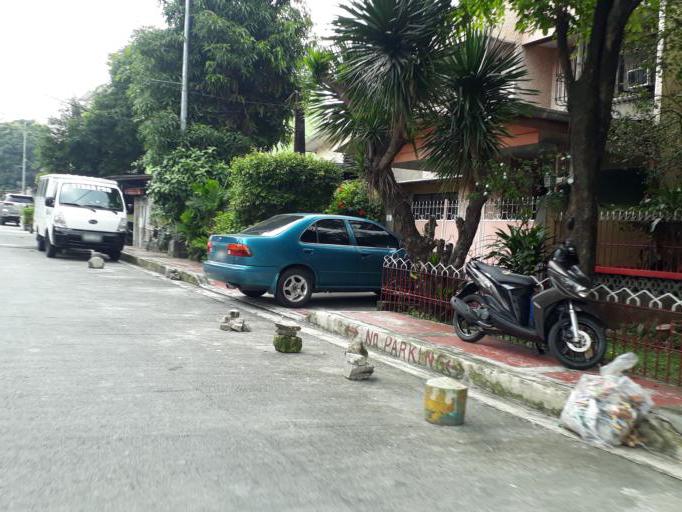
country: PH
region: Calabarzon
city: Bagong Pagasa
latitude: 14.6615
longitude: 121.0313
